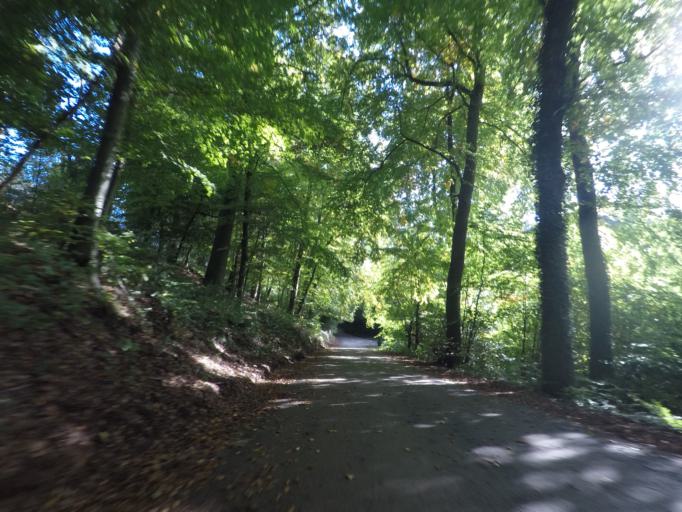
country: LU
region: Luxembourg
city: Itzig
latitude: 49.5955
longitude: 6.1736
